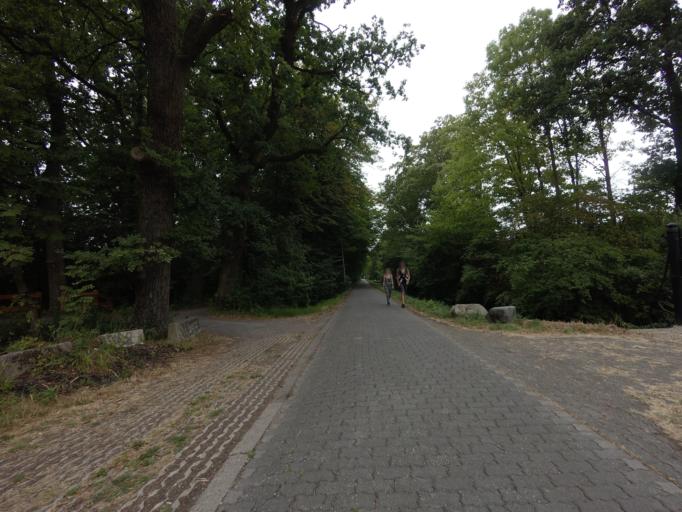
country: NL
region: Utrecht
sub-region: Stichtse Vecht
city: Maarssen
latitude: 52.1255
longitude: 5.0788
